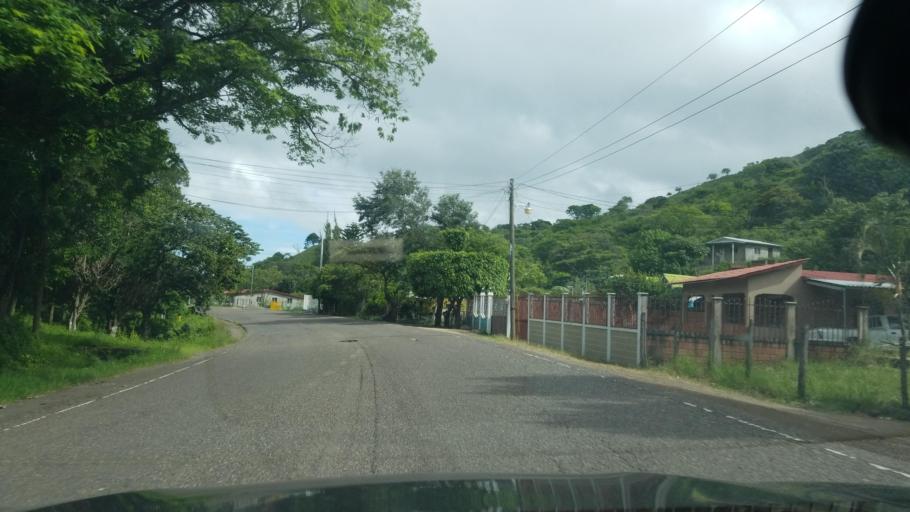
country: HN
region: Choluteca
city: Corpus
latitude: 13.3711
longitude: -86.9605
